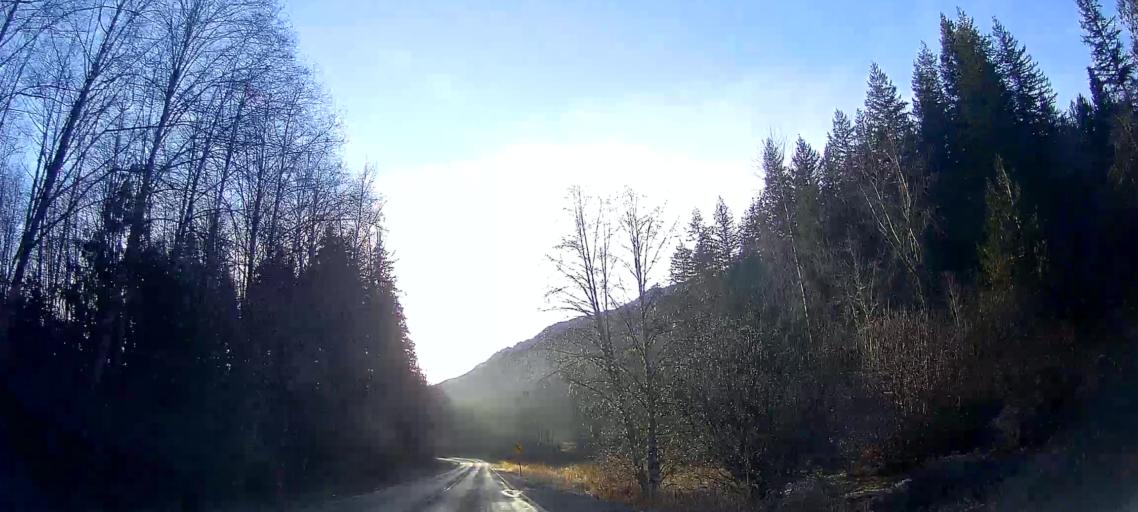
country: US
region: Washington
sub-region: Snohomish County
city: Darrington
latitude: 48.6029
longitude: -121.7627
